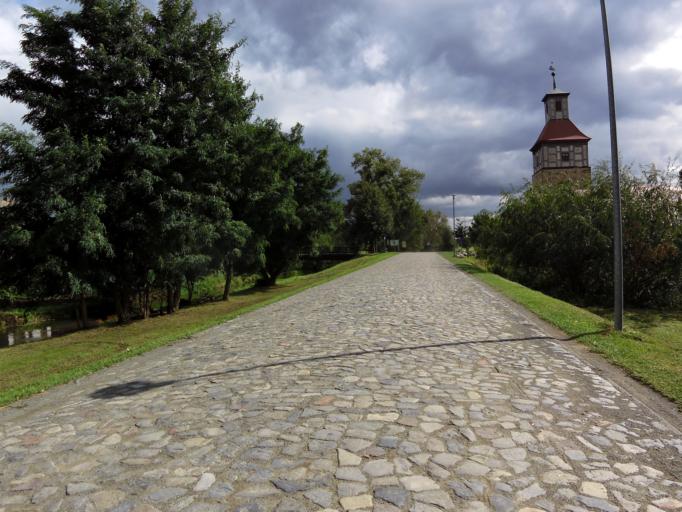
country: DE
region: Saxony-Anhalt
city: Barby
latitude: 51.9652
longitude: 11.9359
